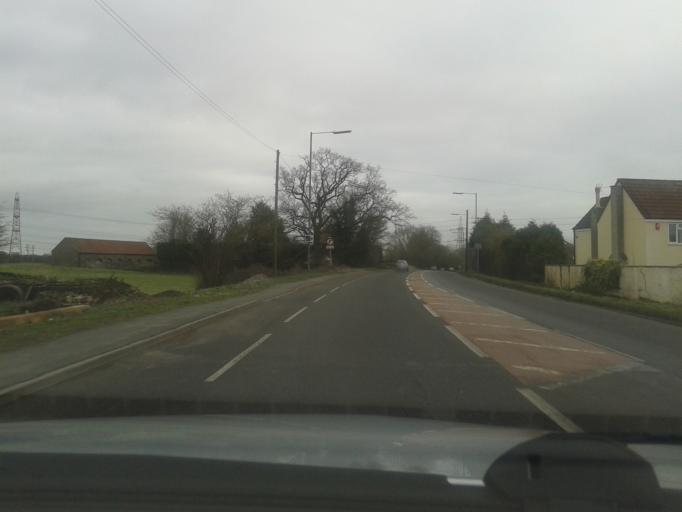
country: GB
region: England
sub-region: South Gloucestershire
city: Yate
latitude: 51.5361
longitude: -2.4557
